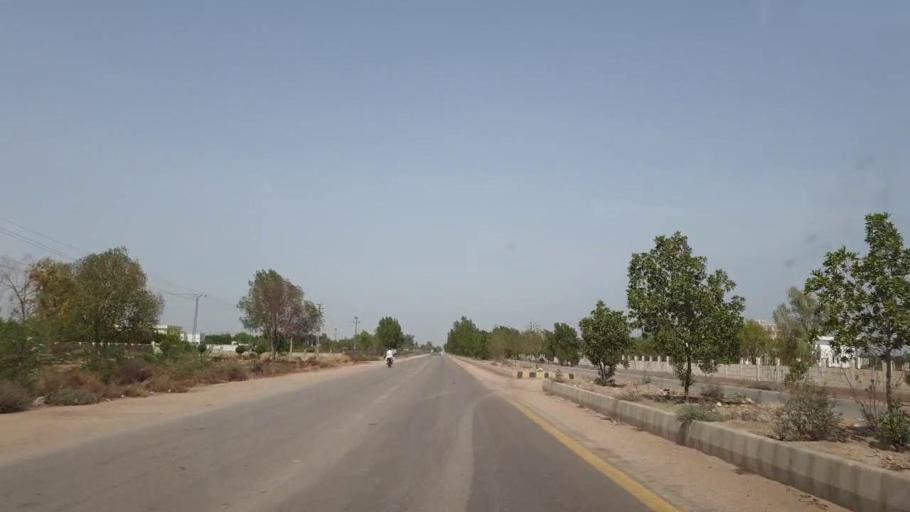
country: PK
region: Sindh
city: Nawabshah
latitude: 26.2331
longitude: 68.3790
